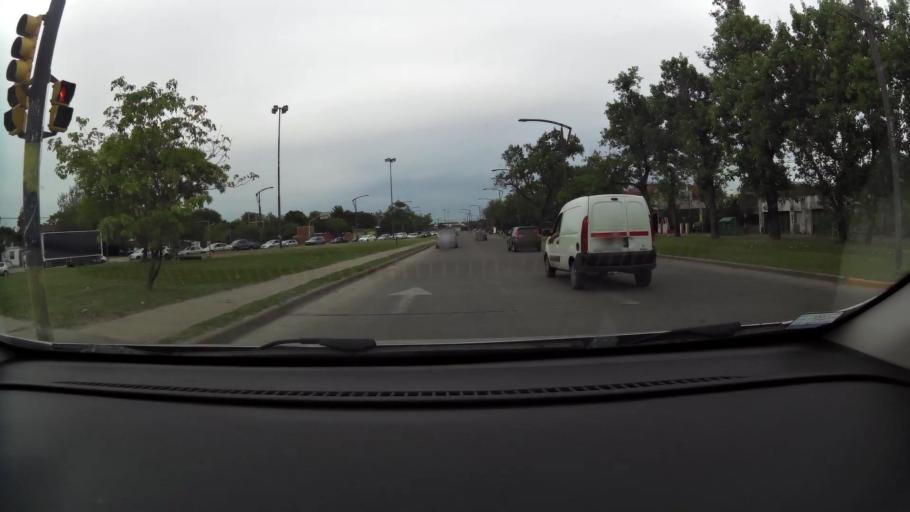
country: AR
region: Santa Fe
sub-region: Departamento de Rosario
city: Rosario
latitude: -32.9141
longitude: -60.6916
